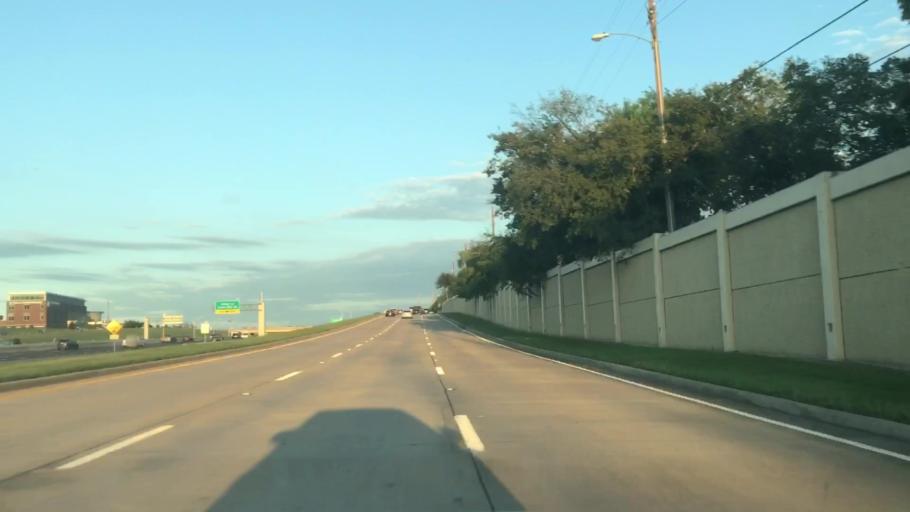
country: US
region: Texas
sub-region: Dallas County
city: Carrollton
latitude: 32.9833
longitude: -96.9031
